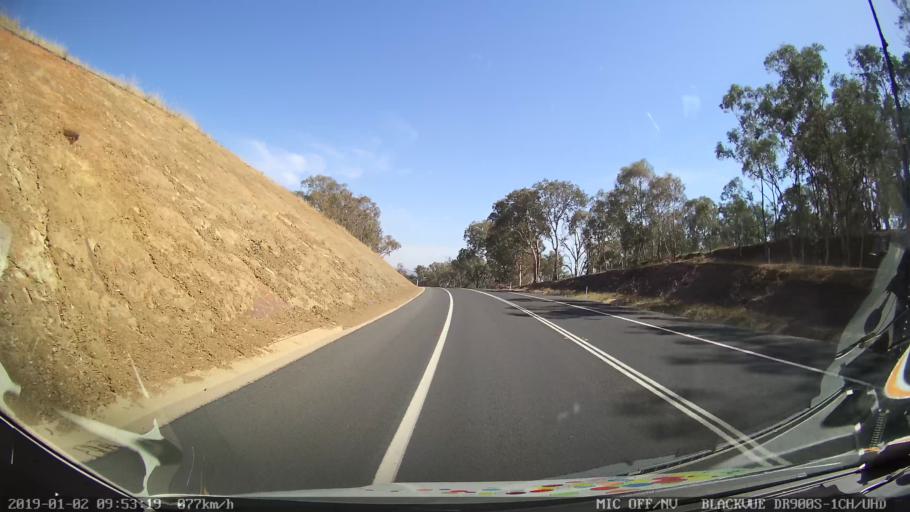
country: AU
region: New South Wales
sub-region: Tumut Shire
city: Tumut
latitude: -35.2492
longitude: 148.2033
